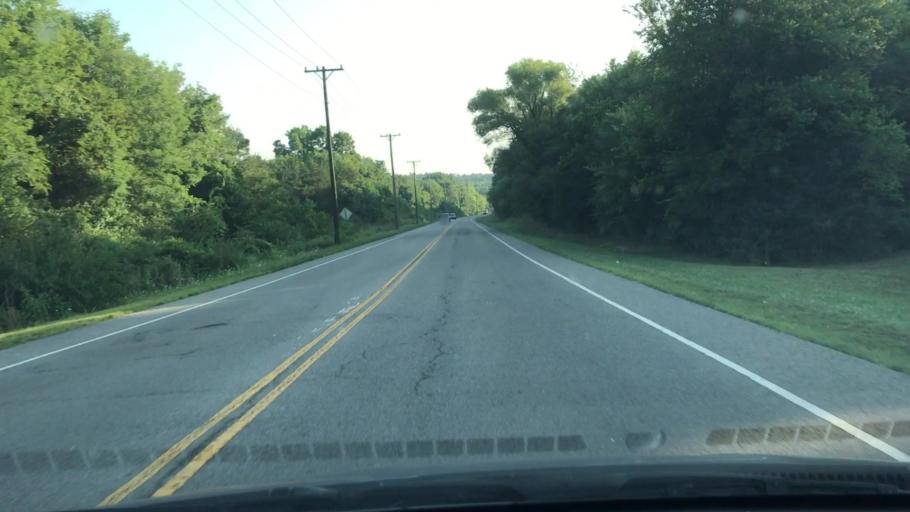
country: US
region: Tennessee
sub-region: Rutherford County
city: La Vergne
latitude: 35.9954
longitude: -86.6243
